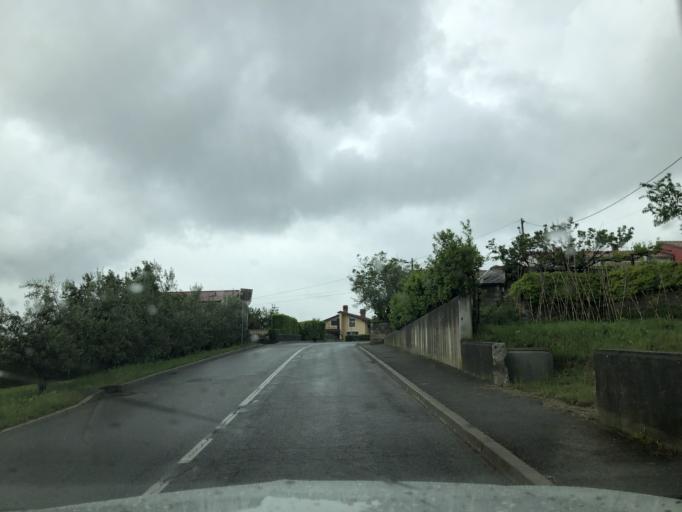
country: SI
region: Koper-Capodistria
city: Pobegi
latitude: 45.5052
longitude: 13.7932
